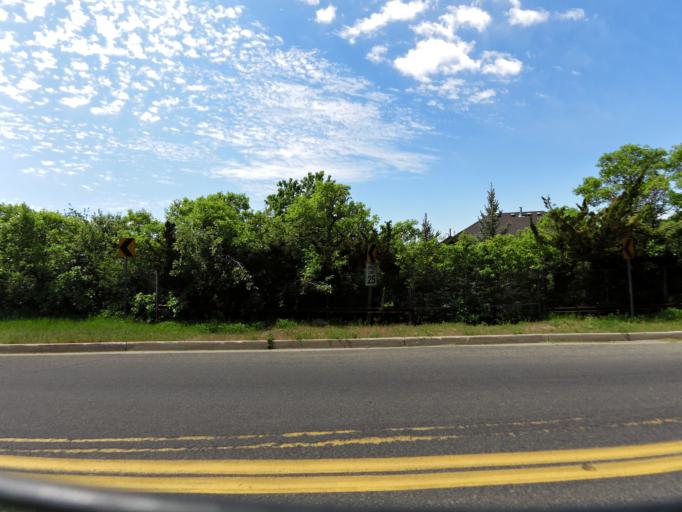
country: US
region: Utah
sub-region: Weber County
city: Uintah
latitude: 41.1757
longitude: -111.9299
